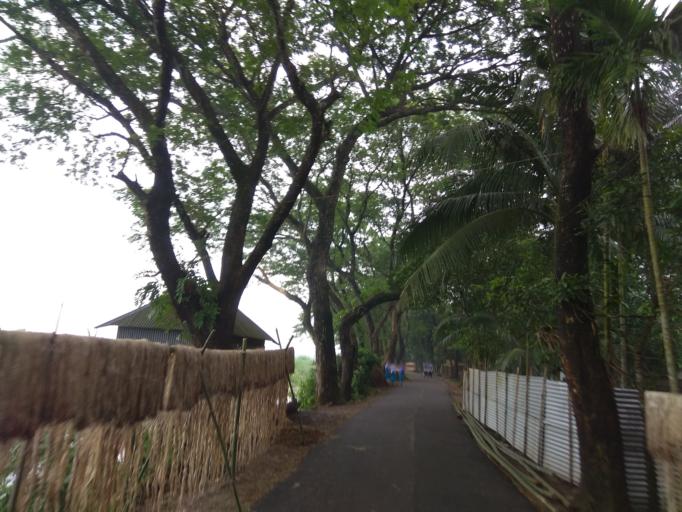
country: BD
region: Dhaka
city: Dohar
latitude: 23.4750
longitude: 90.0587
